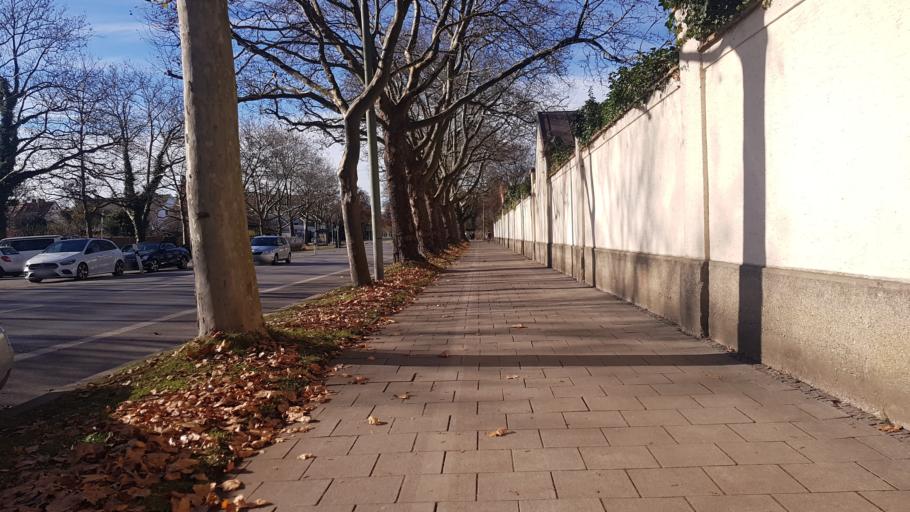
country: DE
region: Bavaria
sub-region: Upper Bavaria
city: Munich
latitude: 48.1689
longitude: 11.5242
